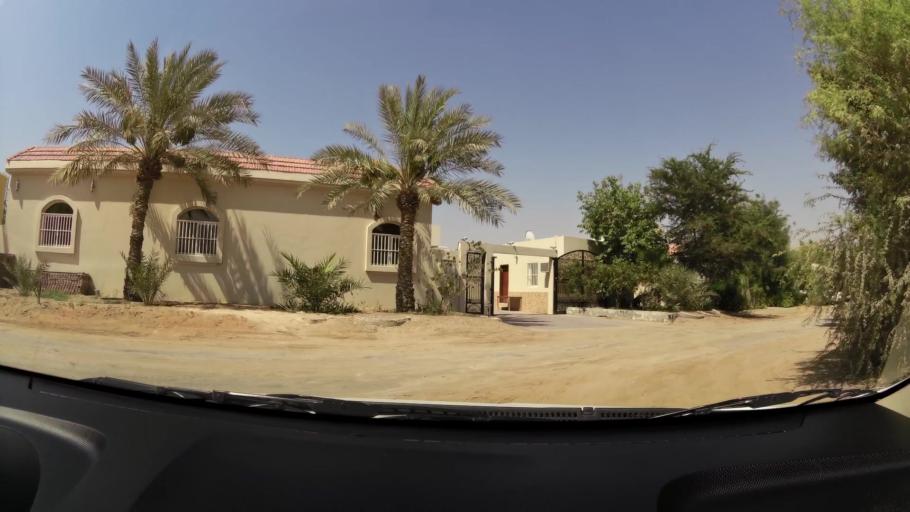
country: AE
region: Ajman
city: Ajman
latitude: 25.4149
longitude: 55.4744
